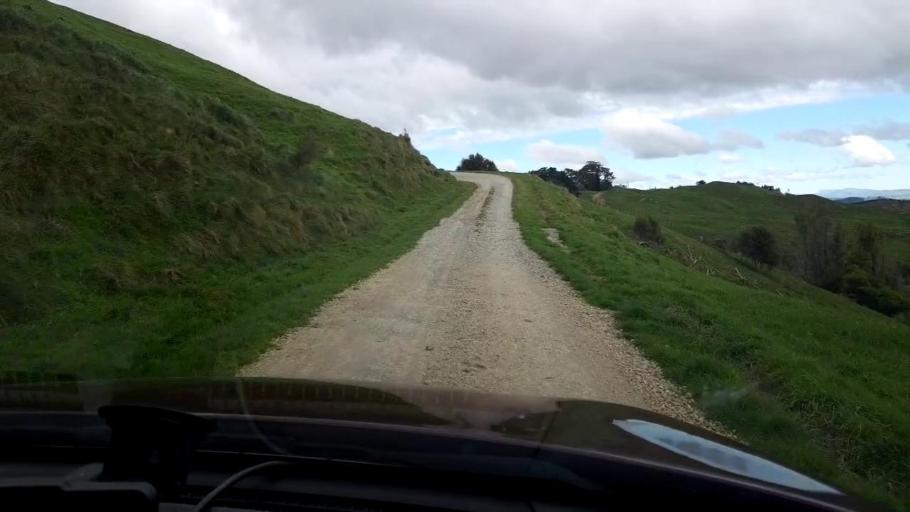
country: NZ
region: Gisborne
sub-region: Gisborne District
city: Gisborne
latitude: -38.3710
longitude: 177.9672
